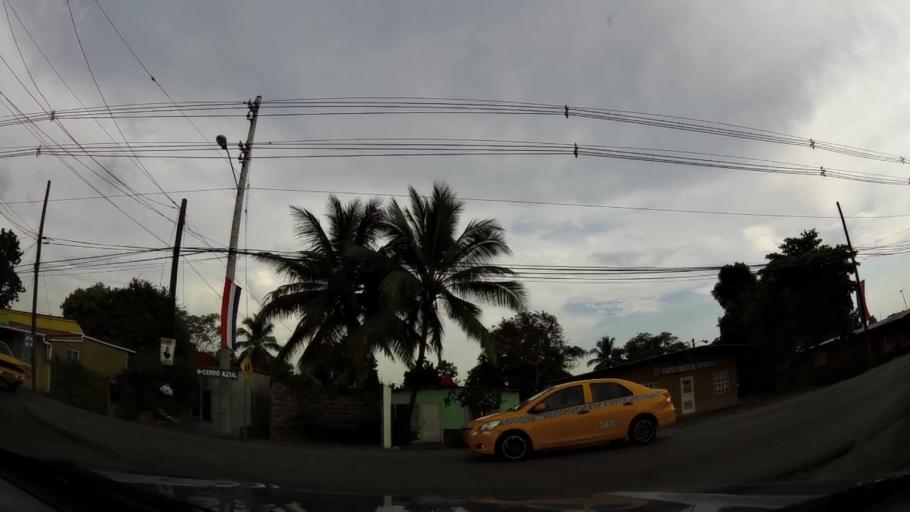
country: PA
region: Panama
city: Tocumen
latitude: 9.1046
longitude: -79.3633
